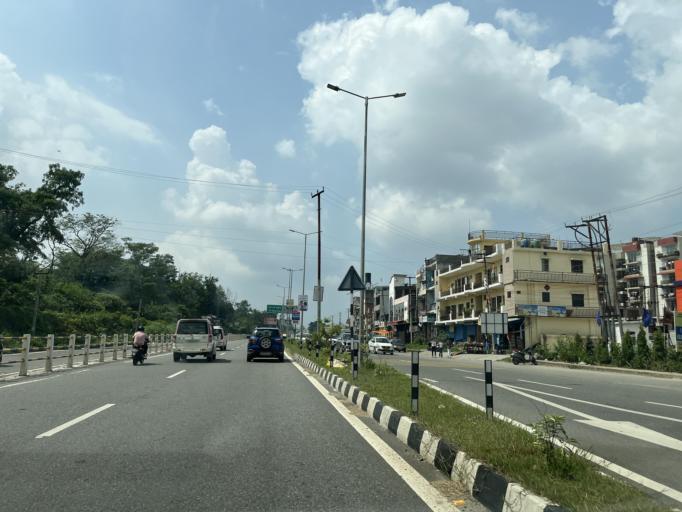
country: IN
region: Uttarakhand
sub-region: Dehradun
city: Raipur
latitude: 30.2713
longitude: 78.0791
